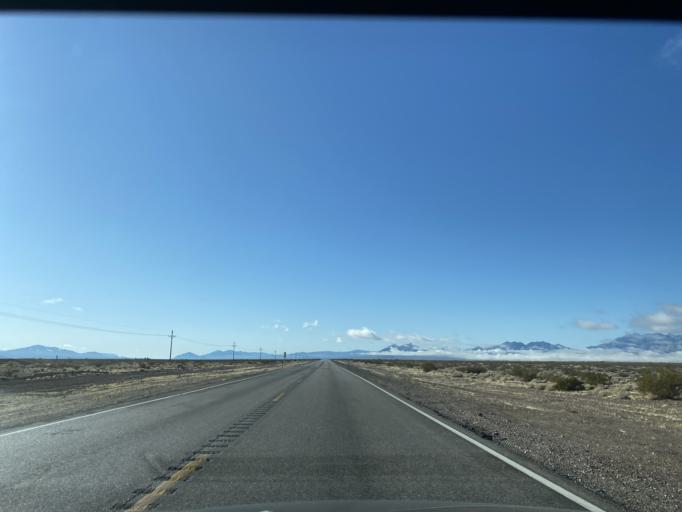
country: US
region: Nevada
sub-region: Nye County
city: Beatty
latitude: 36.5979
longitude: -116.4085
